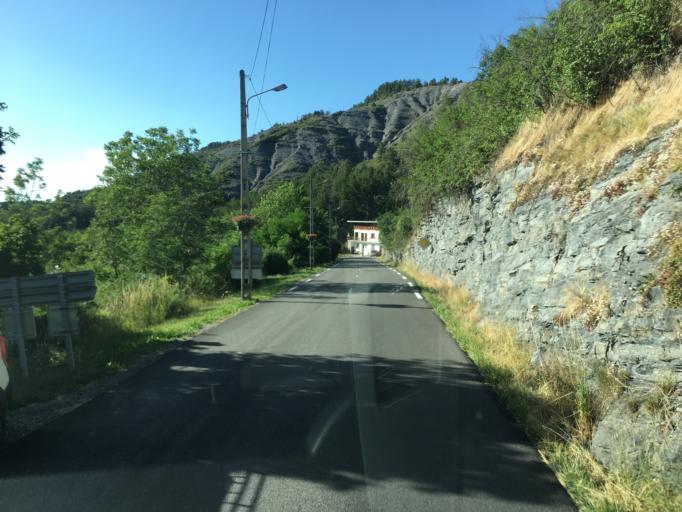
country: FR
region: Provence-Alpes-Cote d'Azur
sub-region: Departement des Alpes-de-Haute-Provence
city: Seyne-les-Alpes
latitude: 44.3504
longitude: 6.3526
